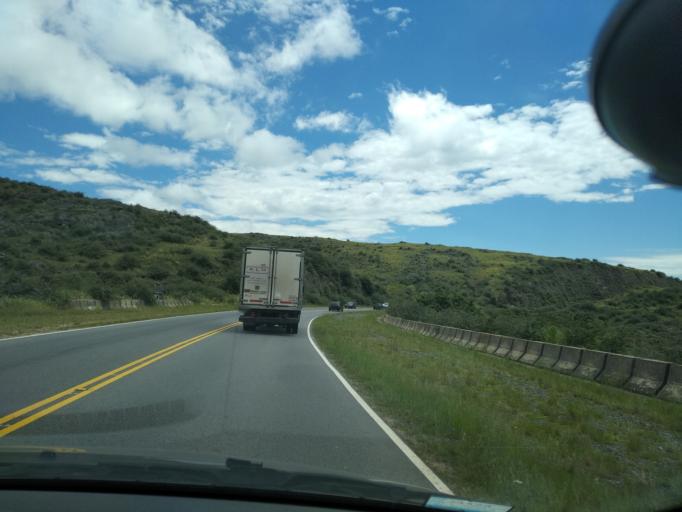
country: AR
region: Cordoba
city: Cuesta Blanca
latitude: -31.6246
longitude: -64.6727
